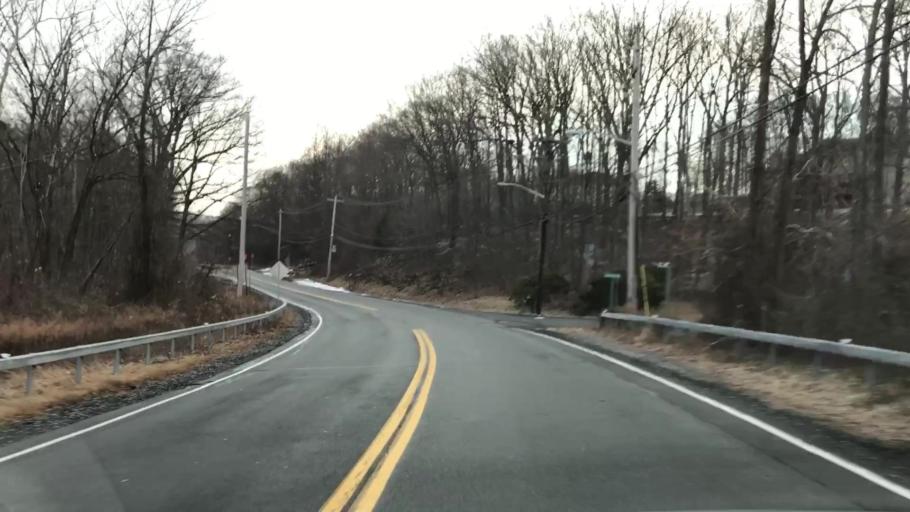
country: US
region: New York
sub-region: Rockland County
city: Thiells
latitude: 41.2353
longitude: -74.0323
